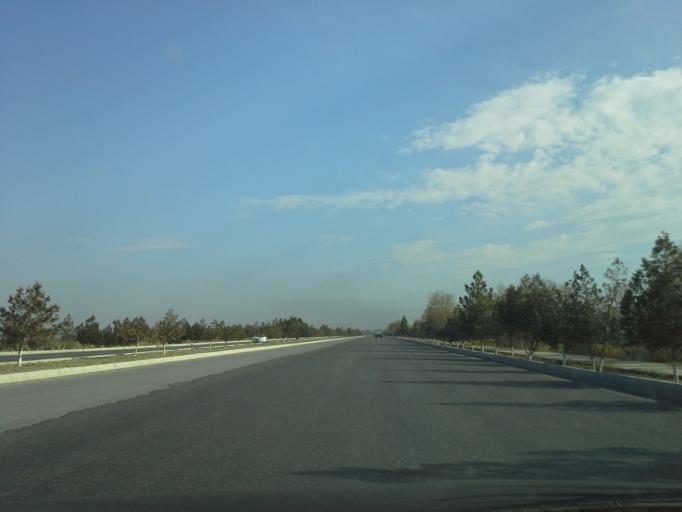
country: TM
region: Ahal
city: Abadan
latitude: 38.0795
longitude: 58.2265
